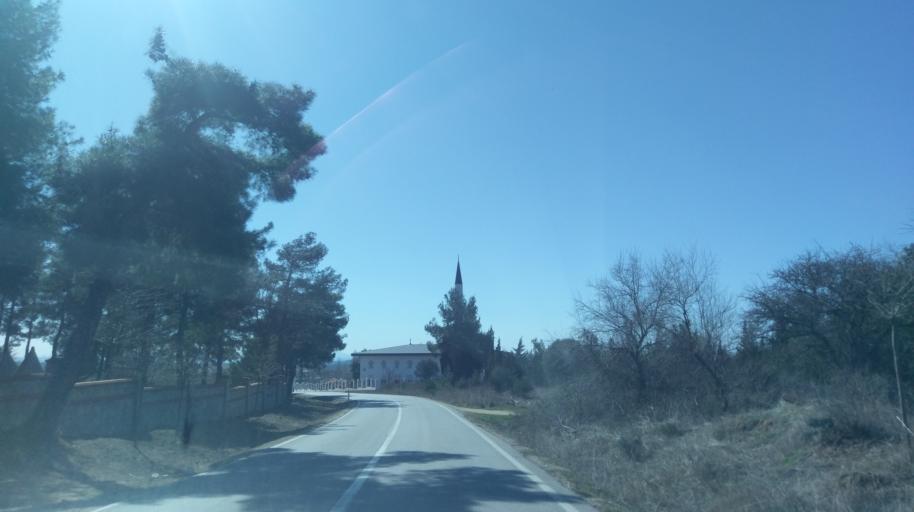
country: TR
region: Canakkale
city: Intepe
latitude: 40.0986
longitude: 26.2274
